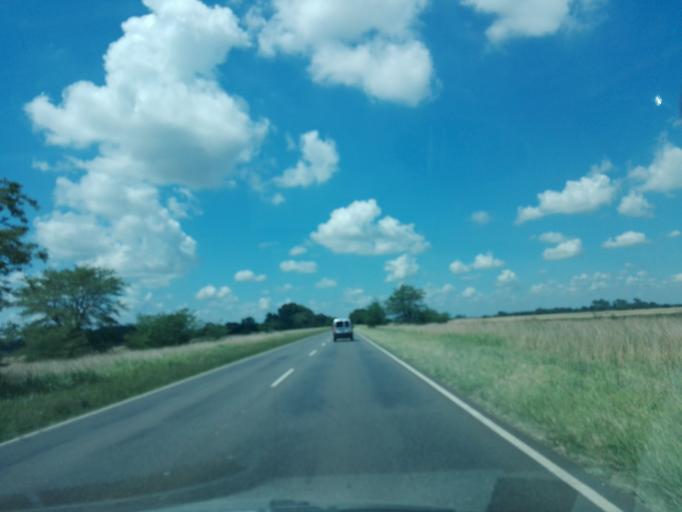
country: AR
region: Buenos Aires
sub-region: Partido de General Belgrano
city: General Belgrano
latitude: -35.8710
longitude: -58.6179
